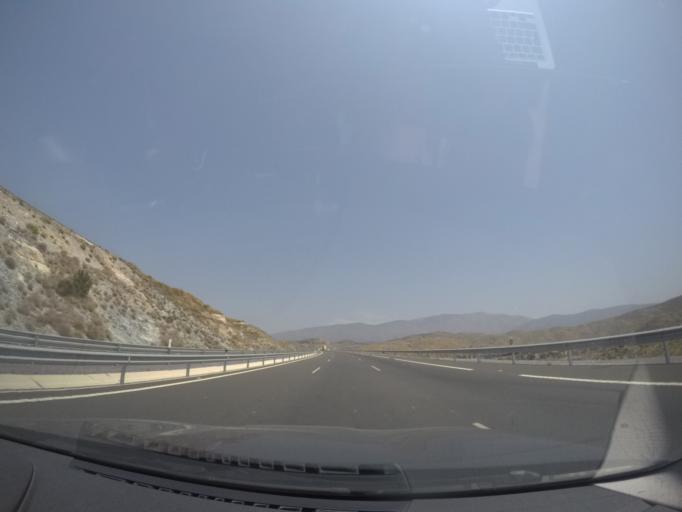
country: ES
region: Andalusia
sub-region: Provincia de Granada
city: Motril
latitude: 36.7527
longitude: -3.4849
